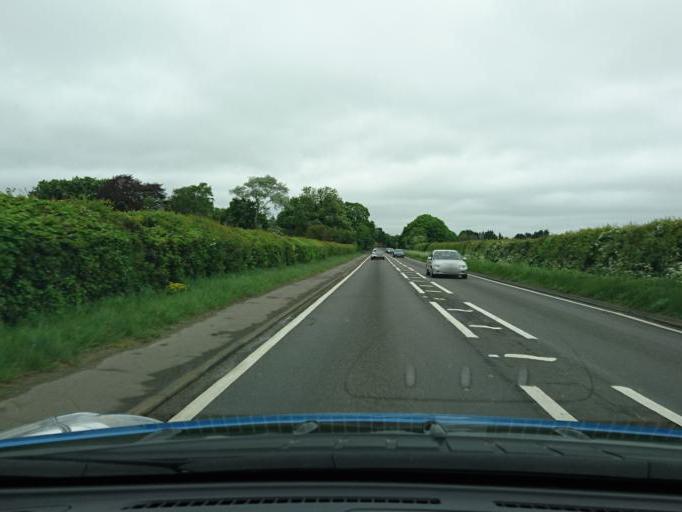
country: GB
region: England
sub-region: Oxfordshire
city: Boars Hill
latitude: 51.7231
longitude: -1.3316
